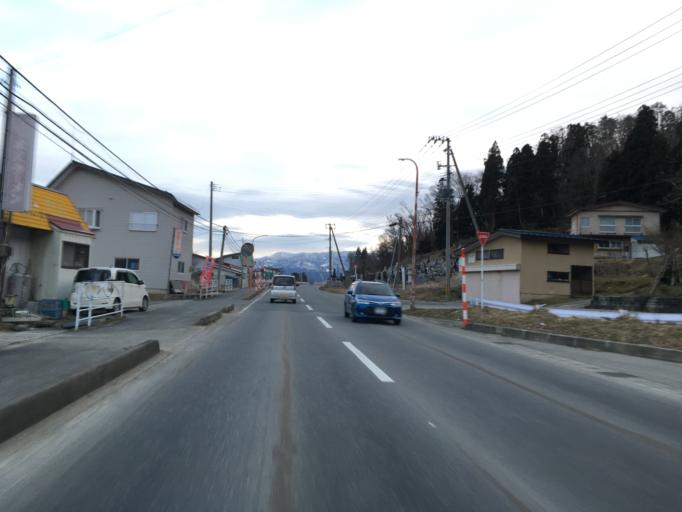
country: JP
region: Yamagata
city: Yonezawa
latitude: 37.9439
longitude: 140.0744
